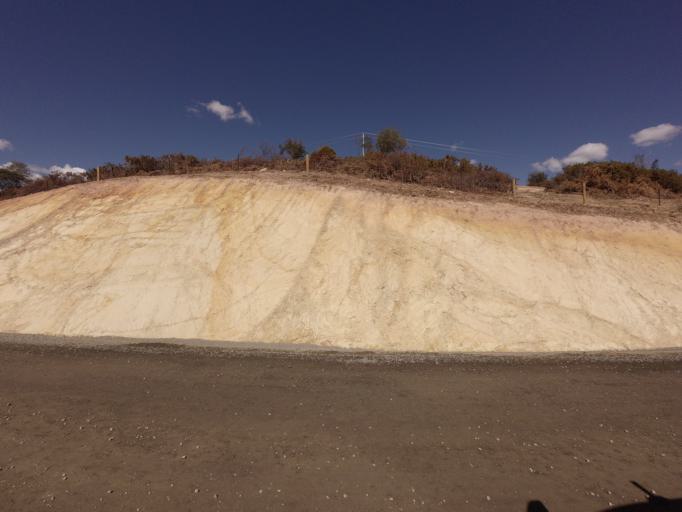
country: AU
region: Tasmania
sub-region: Break O'Day
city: St Helens
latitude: -41.6542
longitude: 147.9238
